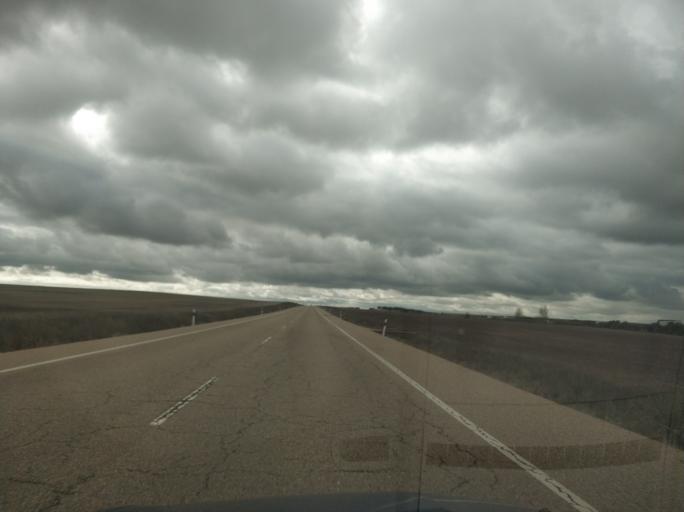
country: ES
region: Castille and Leon
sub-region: Provincia de Valladolid
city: Alaejos
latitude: 41.2800
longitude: -5.2479
